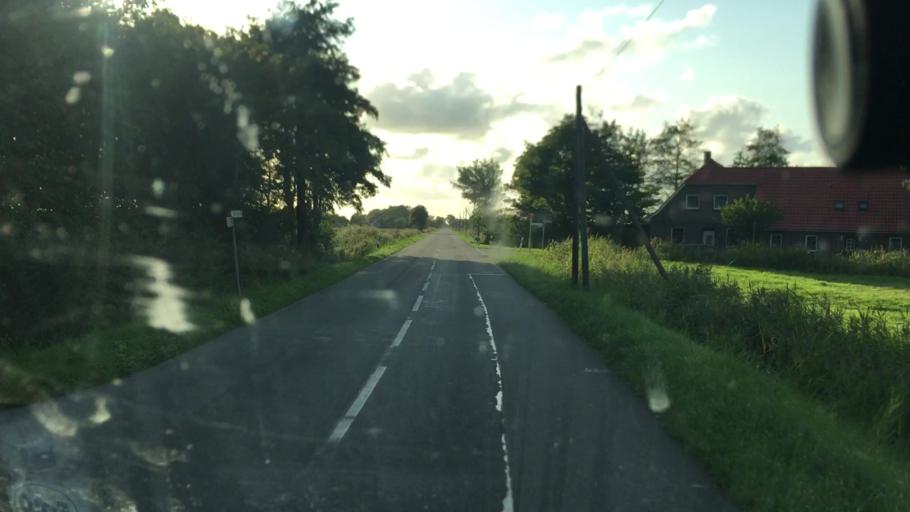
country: DE
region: Lower Saxony
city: Werdum
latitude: 53.6597
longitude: 7.7729
